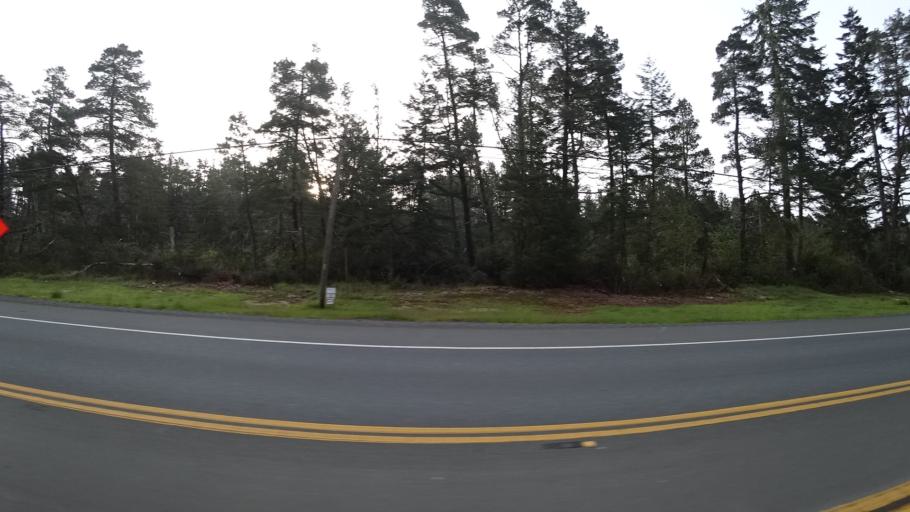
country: US
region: Oregon
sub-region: Coos County
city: Lakeside
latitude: 43.5995
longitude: -124.1802
